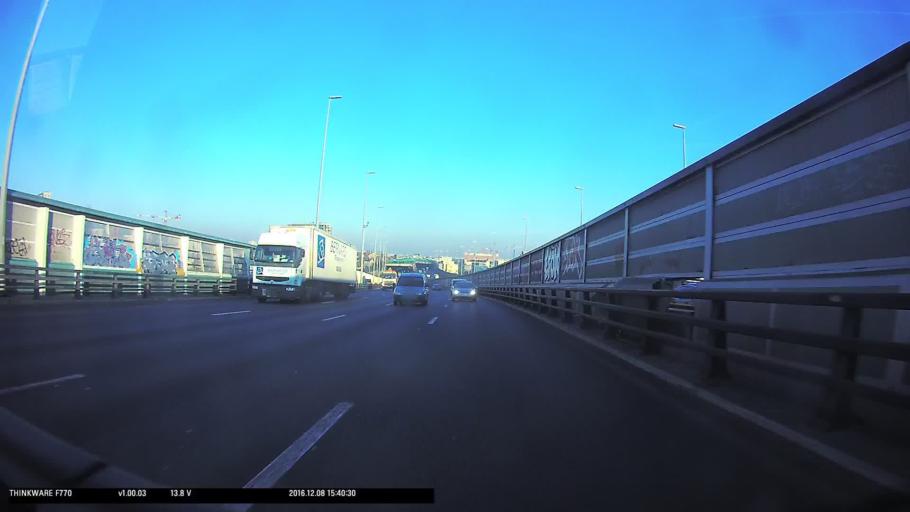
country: FR
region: Ile-de-France
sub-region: Departement de Seine-Saint-Denis
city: Aubervilliers
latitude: 48.9213
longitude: 2.3751
